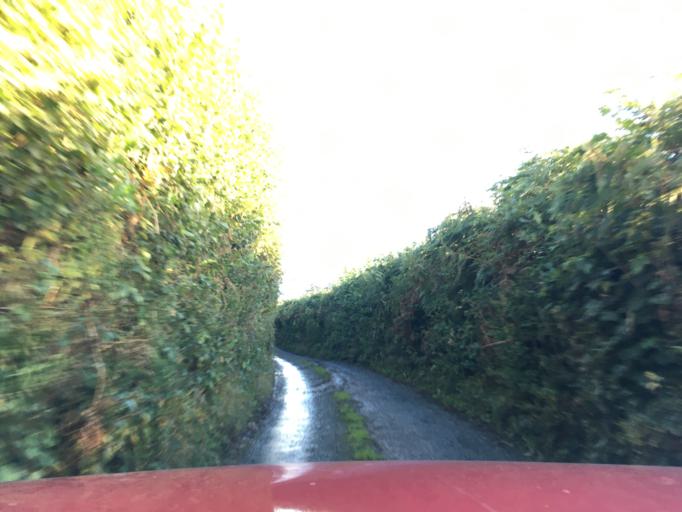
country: GB
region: England
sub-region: Devon
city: Dartmouth
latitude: 50.3361
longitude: -3.6027
